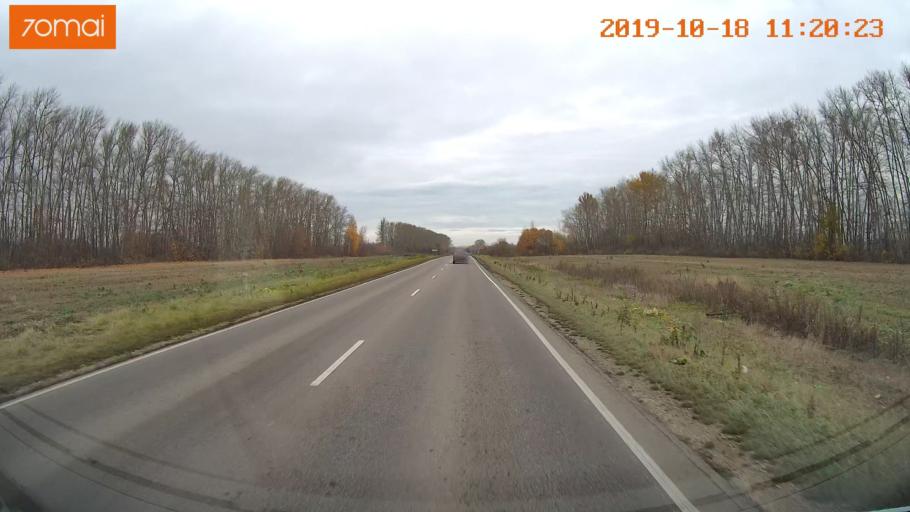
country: RU
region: Tula
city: Kimovsk
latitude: 54.0598
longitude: 38.5583
